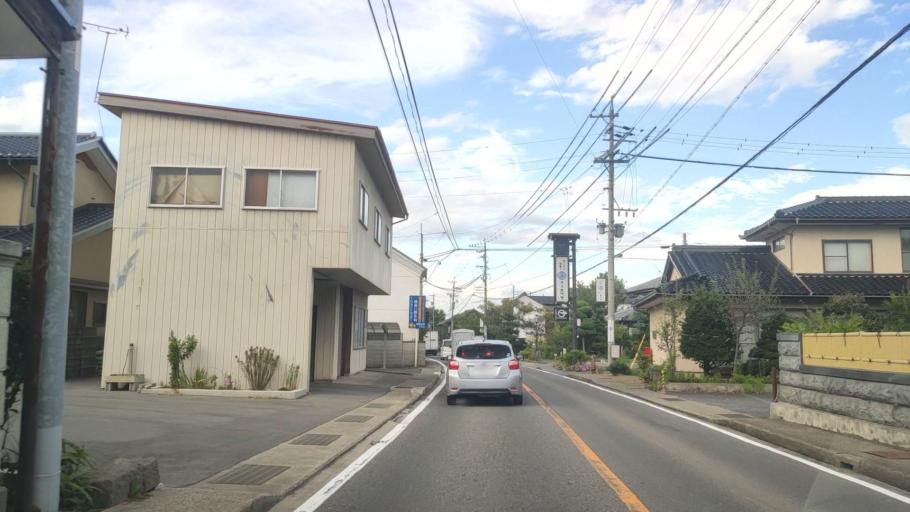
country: JP
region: Nagano
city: Suzaka
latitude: 36.6938
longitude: 138.3155
